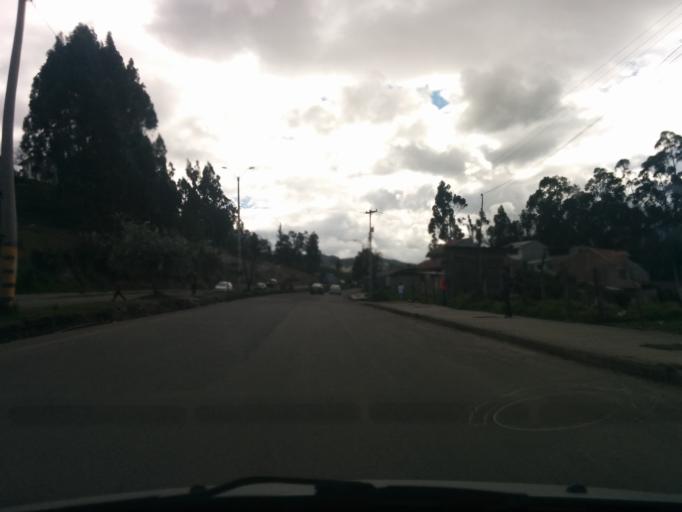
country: EC
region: Azuay
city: Cuenca
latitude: -2.9230
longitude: -79.0291
